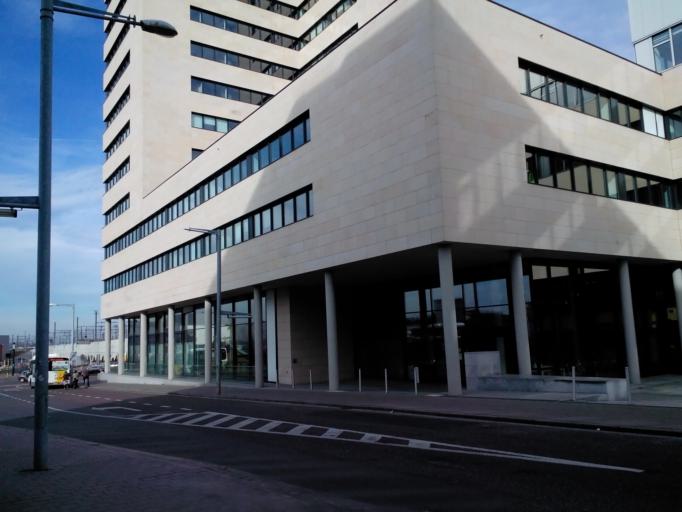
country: BE
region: Flanders
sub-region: Provincie Vlaams-Brabant
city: Leuven
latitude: 50.8834
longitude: 4.7141
